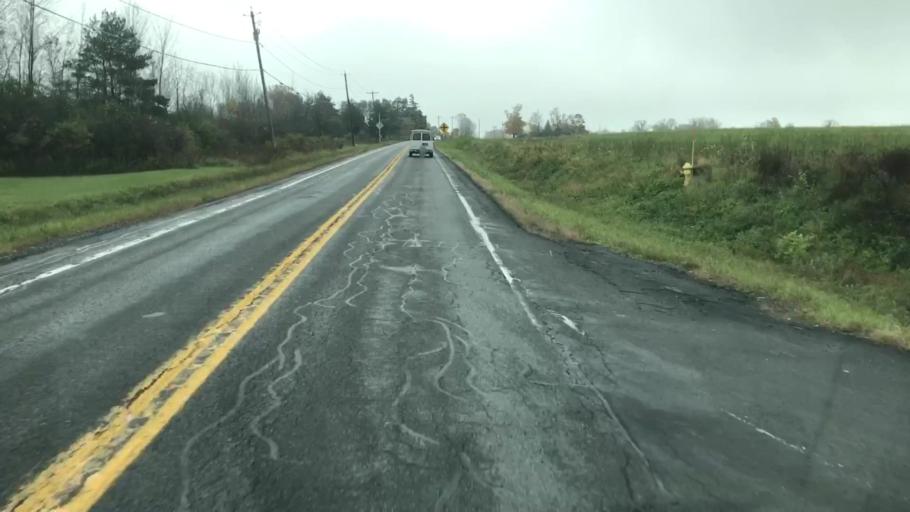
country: US
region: New York
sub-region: Onondaga County
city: Skaneateles
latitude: 42.9760
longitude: -76.4277
